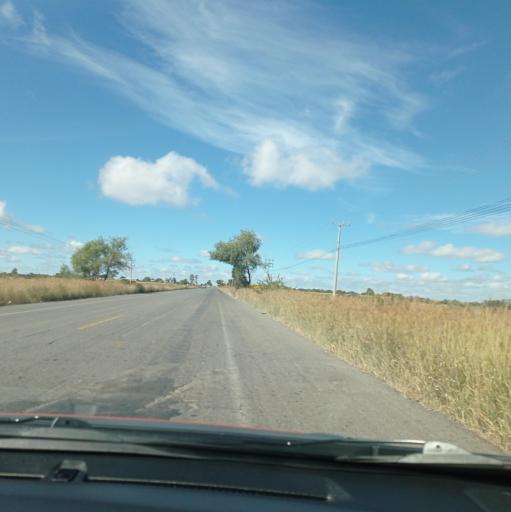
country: MX
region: Jalisco
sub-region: San Julian
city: Colonia Veintitres de Mayo
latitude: 21.0096
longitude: -102.2433
